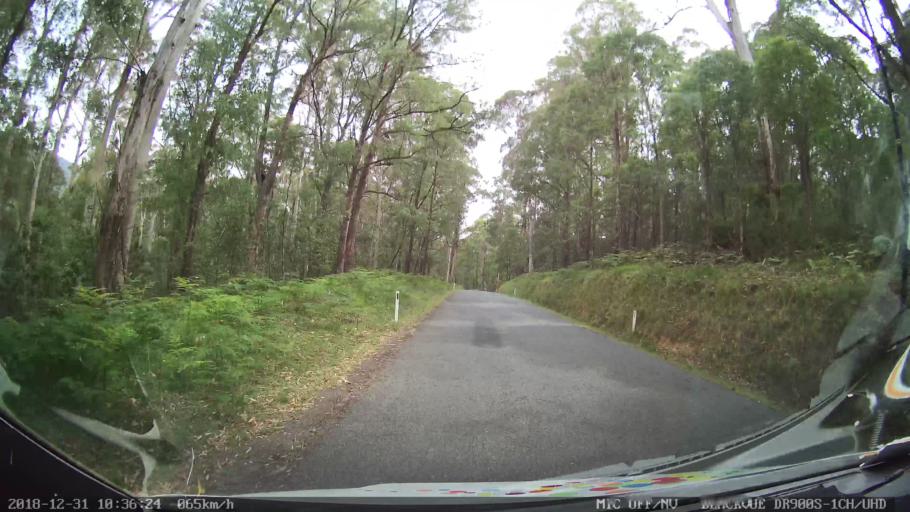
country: AU
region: New South Wales
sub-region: Snowy River
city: Jindabyne
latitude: -36.4265
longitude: 148.1712
